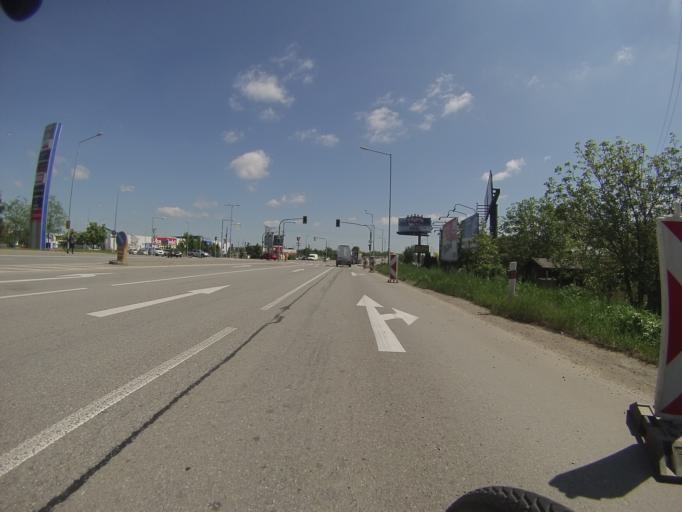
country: CZ
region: South Moravian
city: Modrice
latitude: 49.1335
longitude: 16.6313
